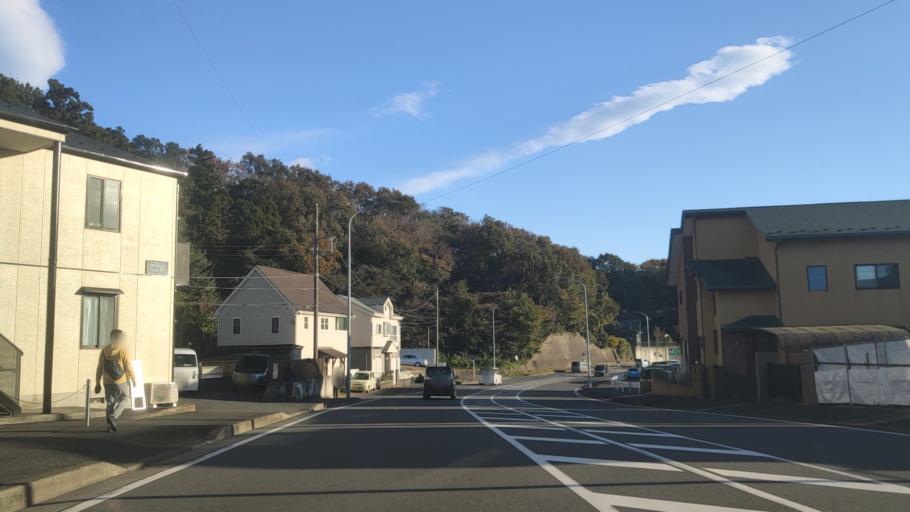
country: JP
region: Kanagawa
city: Fujisawa
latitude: 35.3871
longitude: 139.4996
